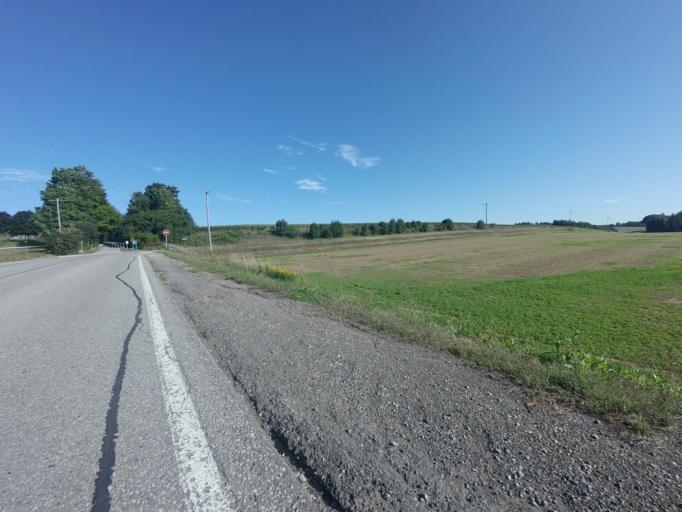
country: CA
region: Ontario
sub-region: Wellington County
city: Guelph
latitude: 43.6522
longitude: -80.4179
